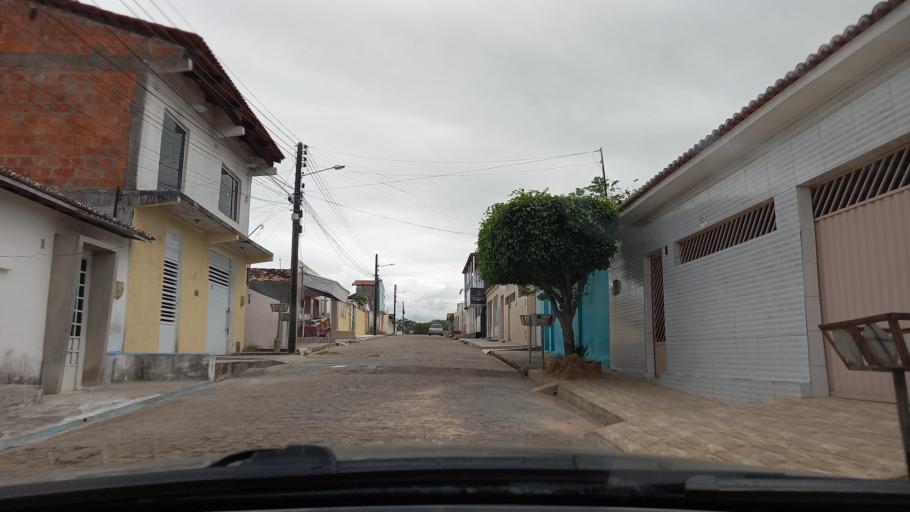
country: BR
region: Sergipe
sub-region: Caninde De Sao Francisco
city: Caninde de Sao Francisco
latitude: -9.6043
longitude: -37.7576
